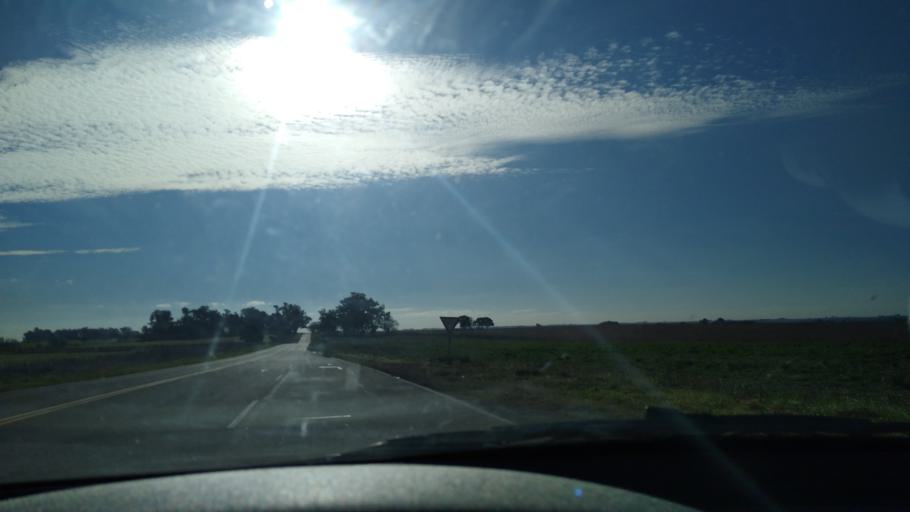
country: AR
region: Entre Rios
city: Aranguren
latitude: -32.3349
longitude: -60.3821
